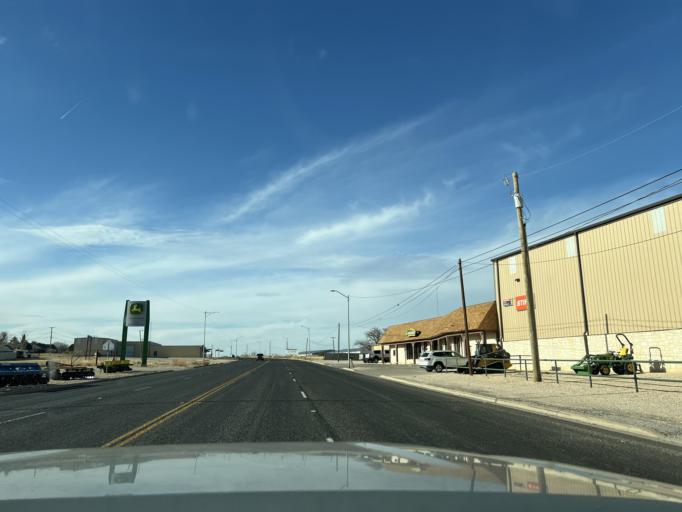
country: US
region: Texas
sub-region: Scurry County
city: Snyder
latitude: 32.7098
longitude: -100.8891
